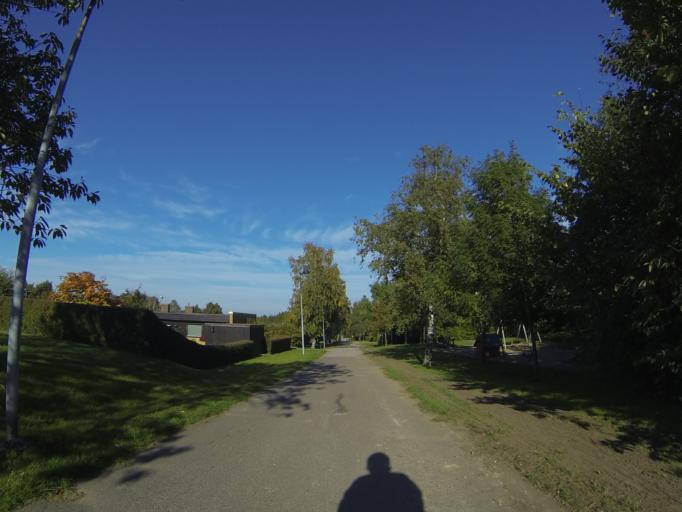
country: SE
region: Skane
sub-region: Lunds Kommun
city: Genarp
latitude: 55.7117
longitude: 13.3394
